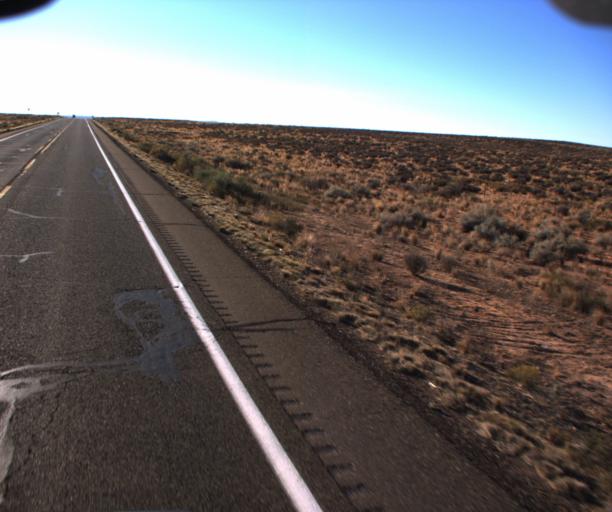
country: US
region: Arizona
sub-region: Coconino County
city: Page
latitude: 36.9675
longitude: -111.5125
